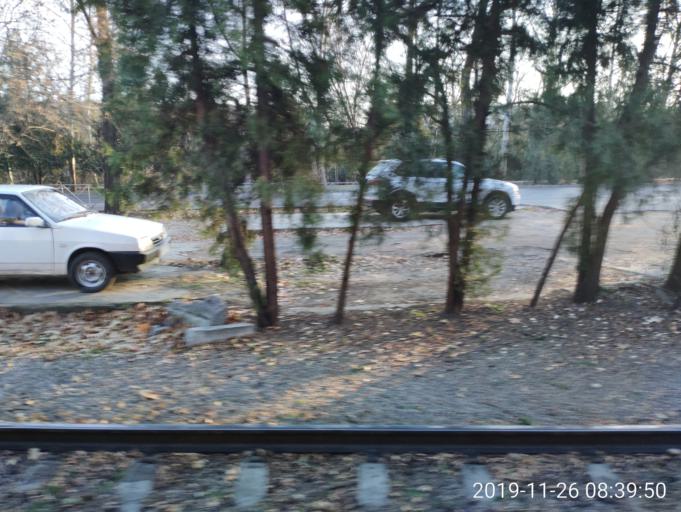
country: RU
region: Krasnodarskiy
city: Krasnodar
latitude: 45.0572
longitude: 38.9847
